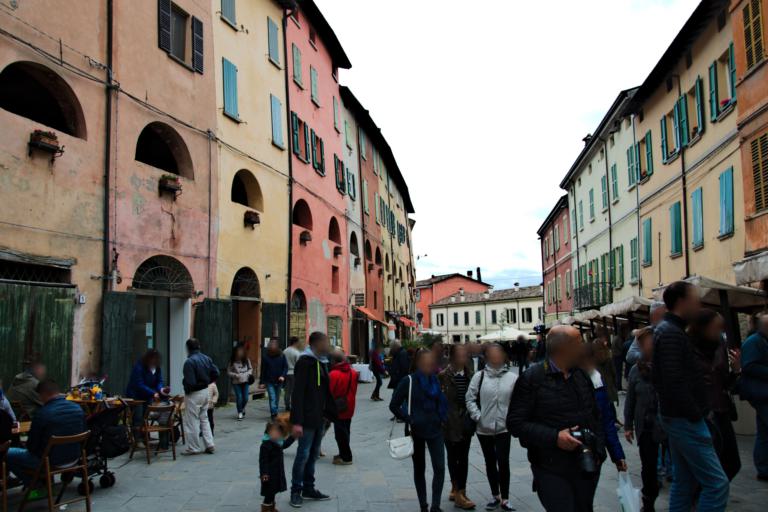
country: IT
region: Emilia-Romagna
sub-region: Provincia di Ravenna
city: Brisighella
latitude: 44.2236
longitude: 11.7732
